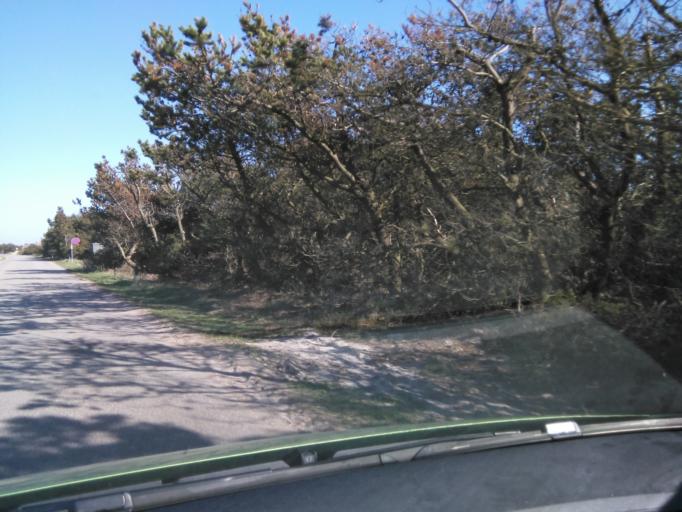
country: DK
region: South Denmark
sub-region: Varde Kommune
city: Oksbol
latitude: 55.5523
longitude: 8.1056
